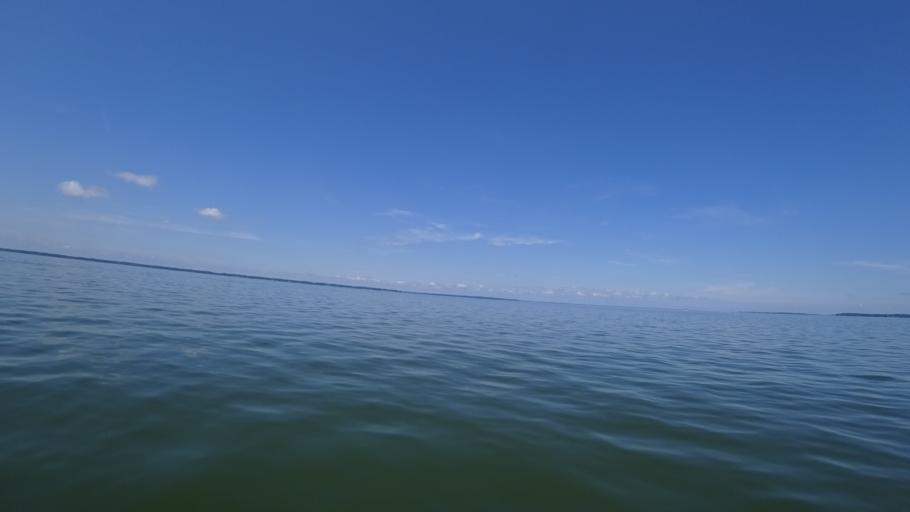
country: US
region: Virginia
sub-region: City of Newport News
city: Newport News
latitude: 37.0068
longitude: -76.4823
